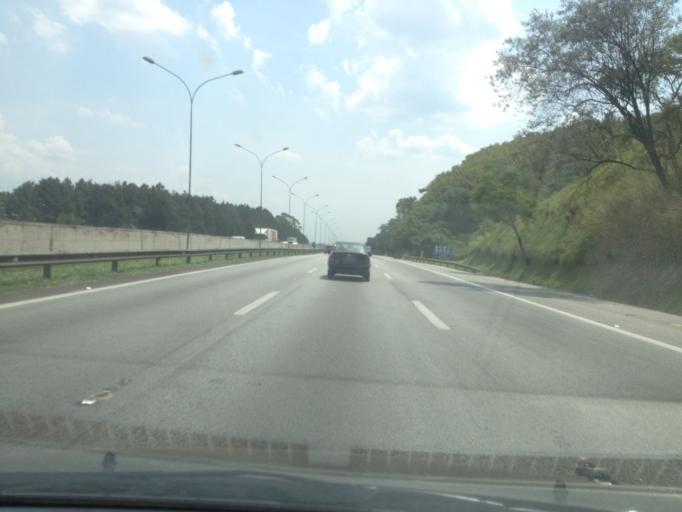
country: BR
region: Sao Paulo
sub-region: Jandira
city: Jandira
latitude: -23.5073
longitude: -46.9015
